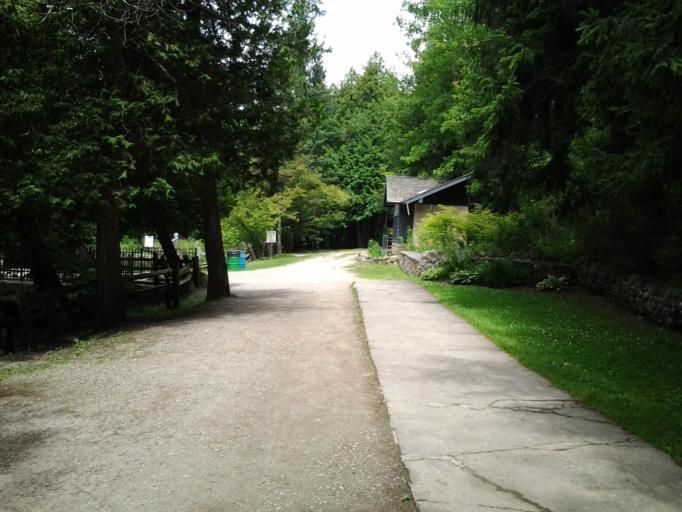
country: CA
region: Ontario
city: Orangeville
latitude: 43.7944
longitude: -80.0116
